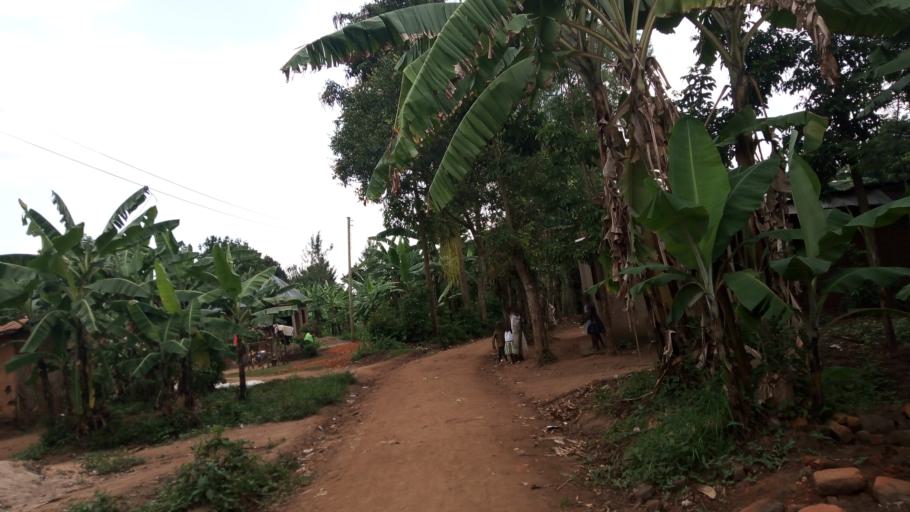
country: UG
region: Eastern Region
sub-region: Mbale District
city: Mbale
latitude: 1.0248
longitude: 34.1743
